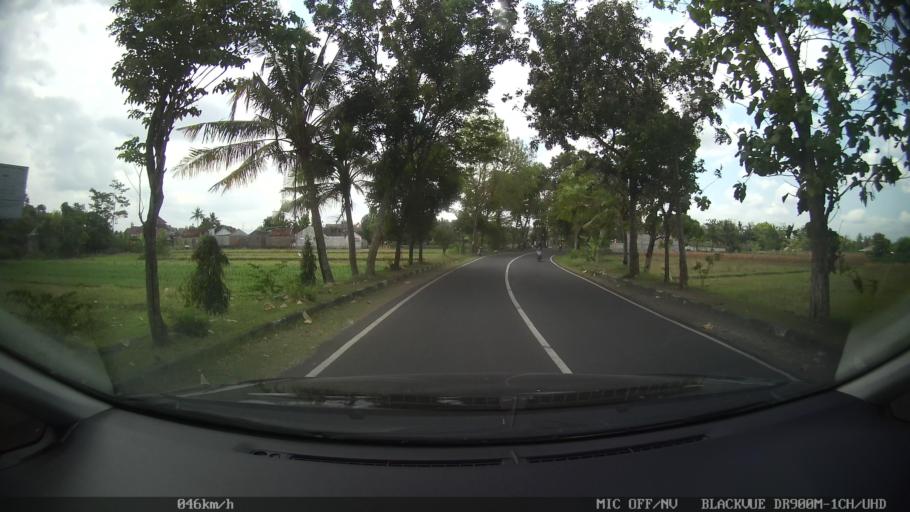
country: ID
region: Daerah Istimewa Yogyakarta
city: Bantul
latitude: -7.8873
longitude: 110.3340
